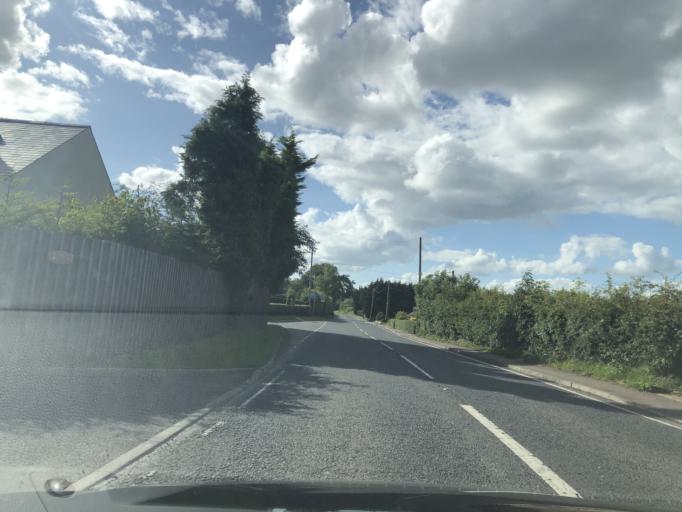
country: GB
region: Northern Ireland
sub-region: Castlereagh District
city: Dundonald
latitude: 54.5742
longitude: -5.7810
